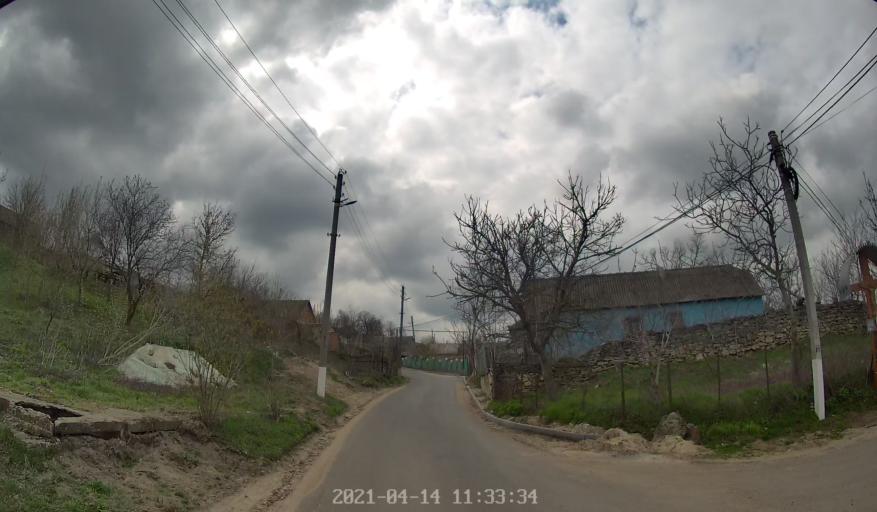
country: MD
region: Criuleni
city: Criuleni
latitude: 47.1793
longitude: 29.1649
